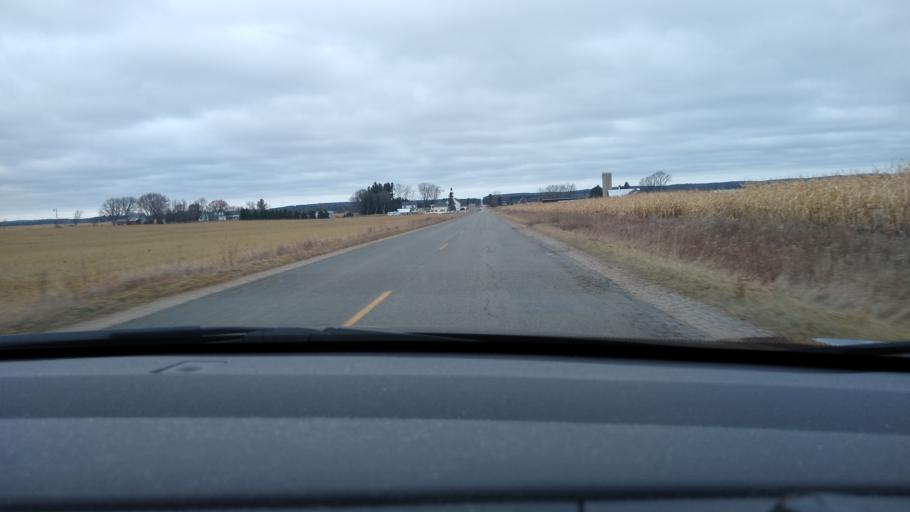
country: US
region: Michigan
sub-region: Missaukee County
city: Lake City
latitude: 44.2383
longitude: -85.0534
